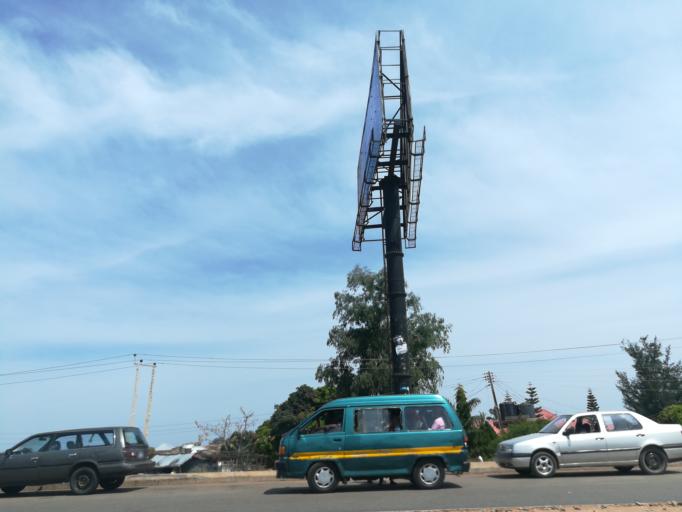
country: NG
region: Plateau
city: Bukuru
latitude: 9.8521
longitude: 8.8670
